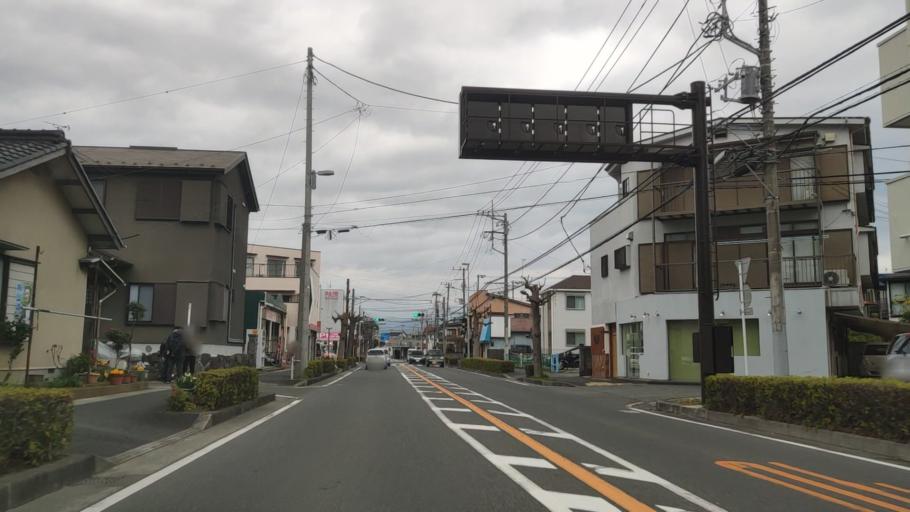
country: JP
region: Kanagawa
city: Odawara
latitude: 35.2731
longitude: 139.1790
